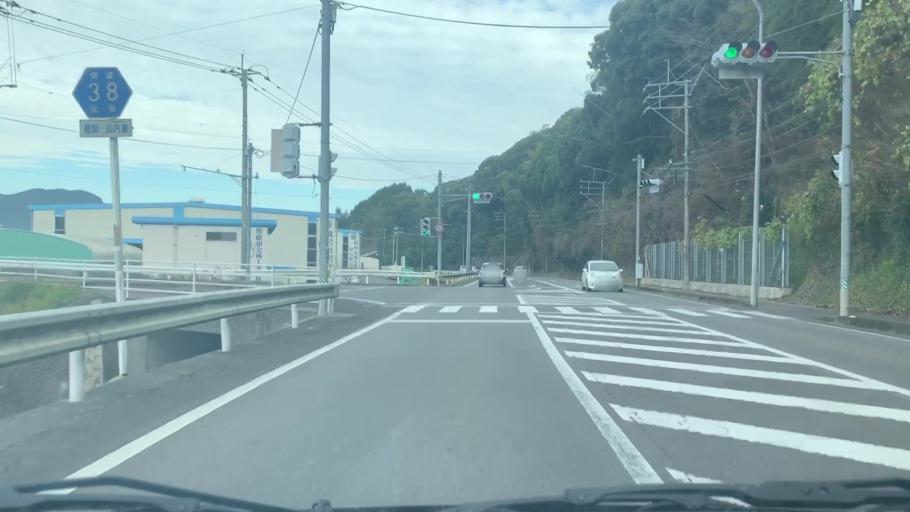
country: JP
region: Saga Prefecture
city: Imaricho-ko
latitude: 33.2869
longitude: 129.9704
